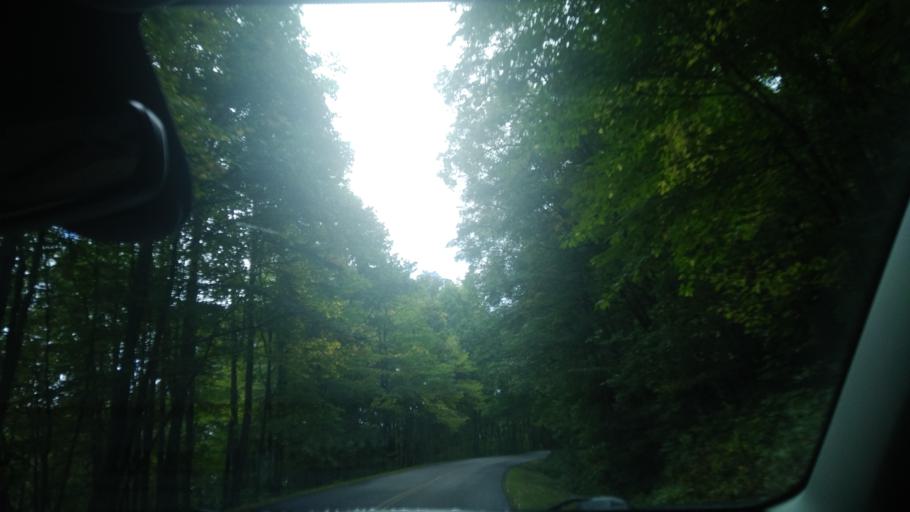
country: US
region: North Carolina
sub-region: Swain County
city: Cherokee
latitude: 35.5219
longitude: -83.2449
